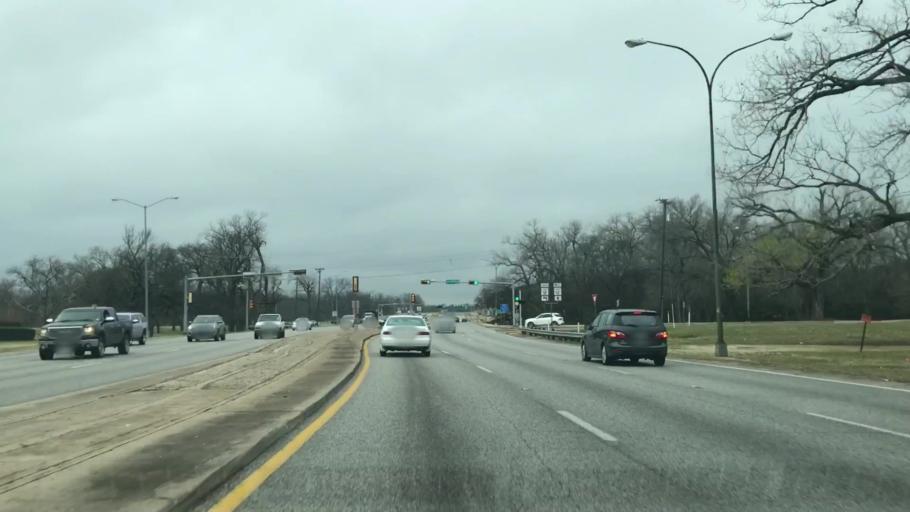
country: US
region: Texas
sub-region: Dallas County
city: Highland Park
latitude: 32.8623
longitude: -96.7170
